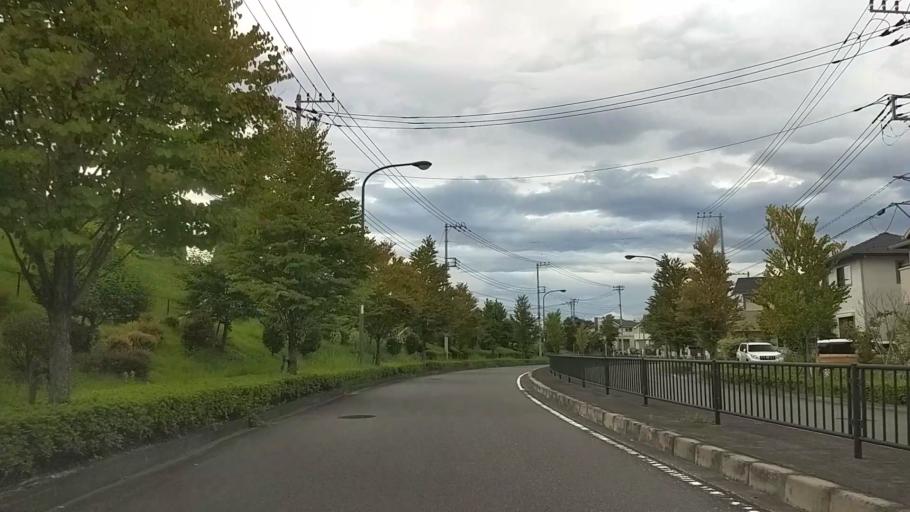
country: JP
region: Tokyo
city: Hachioji
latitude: 35.6170
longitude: 139.3210
